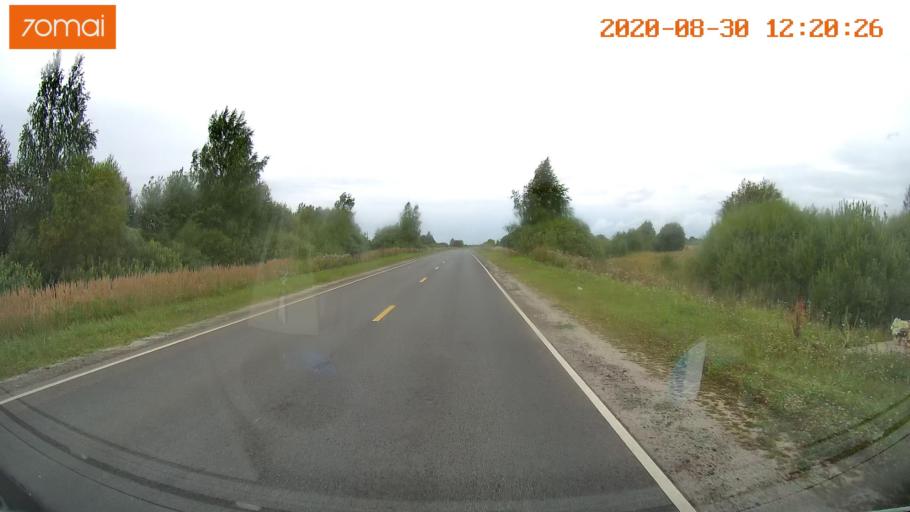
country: RU
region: Ivanovo
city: Yur'yevets
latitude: 57.3228
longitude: 42.9009
